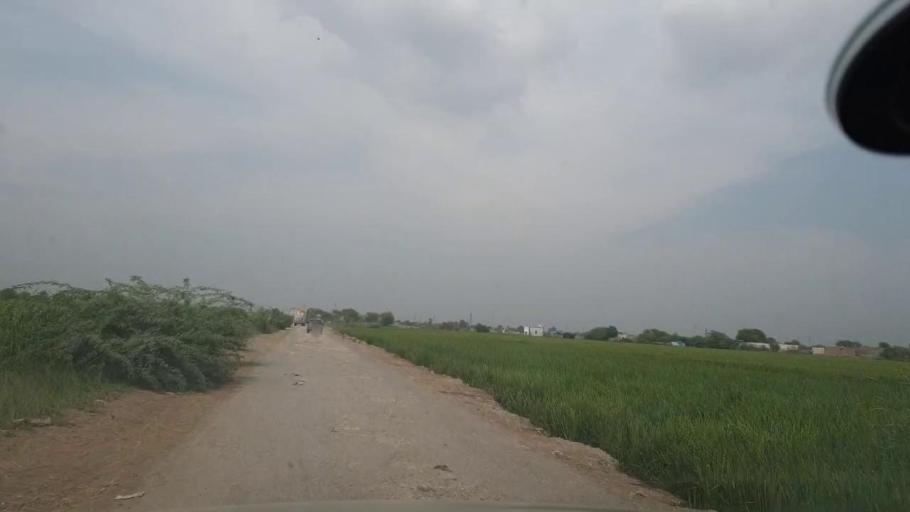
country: PK
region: Sindh
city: Jacobabad
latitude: 28.2549
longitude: 68.4371
